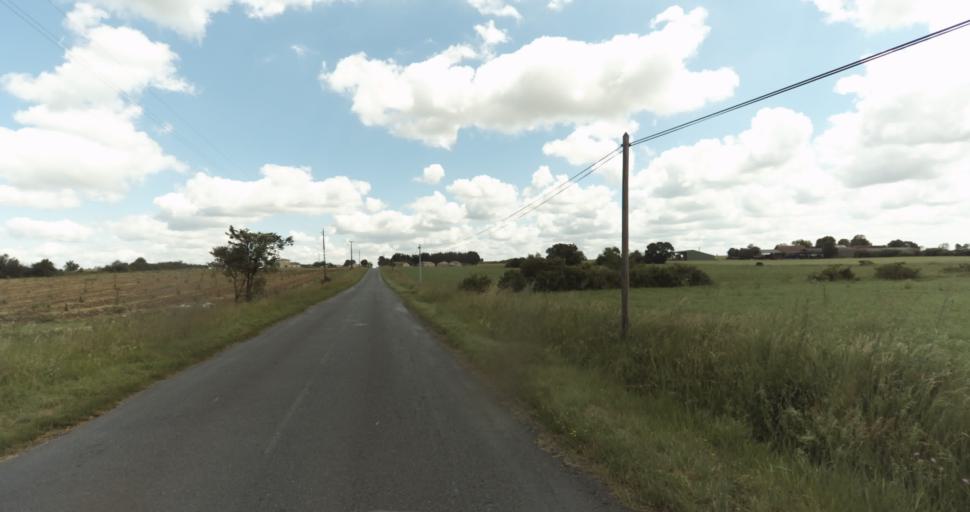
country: FR
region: Aquitaine
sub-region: Departement de la Dordogne
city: Beaumont-du-Perigord
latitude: 44.7564
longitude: 0.7152
